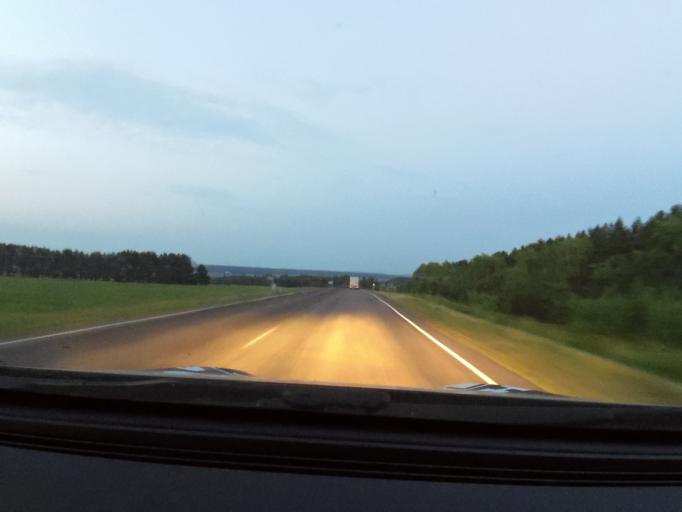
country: RU
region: Bashkortostan
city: Duvan
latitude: 56.0759
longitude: 58.1440
